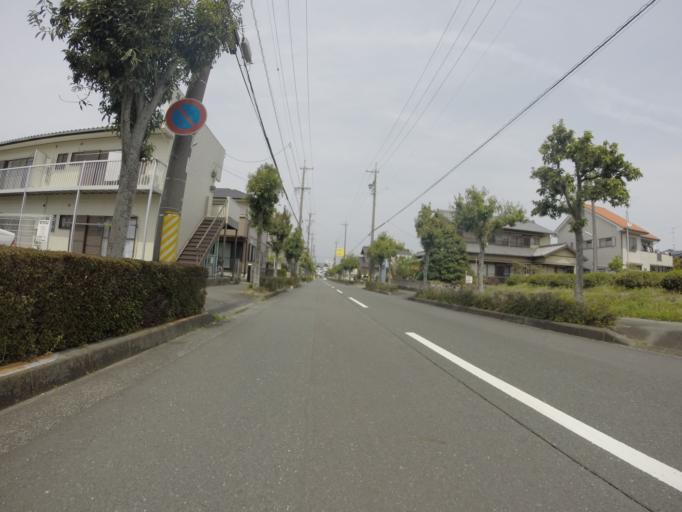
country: JP
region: Shizuoka
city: Kakegawa
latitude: 34.7661
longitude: 138.0179
